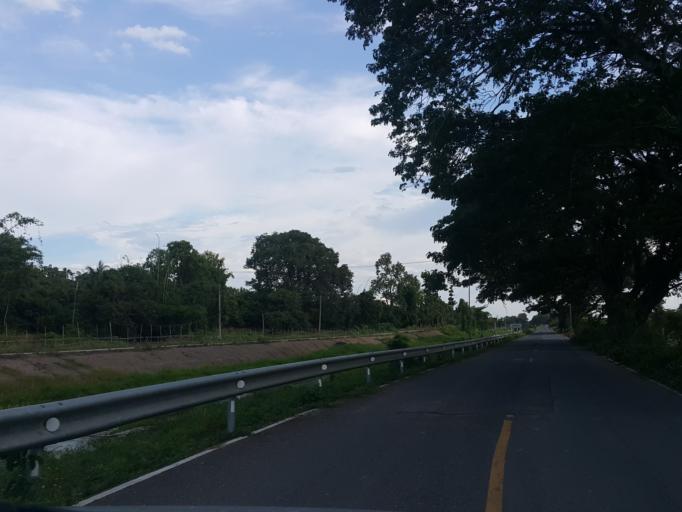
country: TH
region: Chiang Mai
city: Mae Taeng
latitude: 19.0551
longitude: 98.9737
